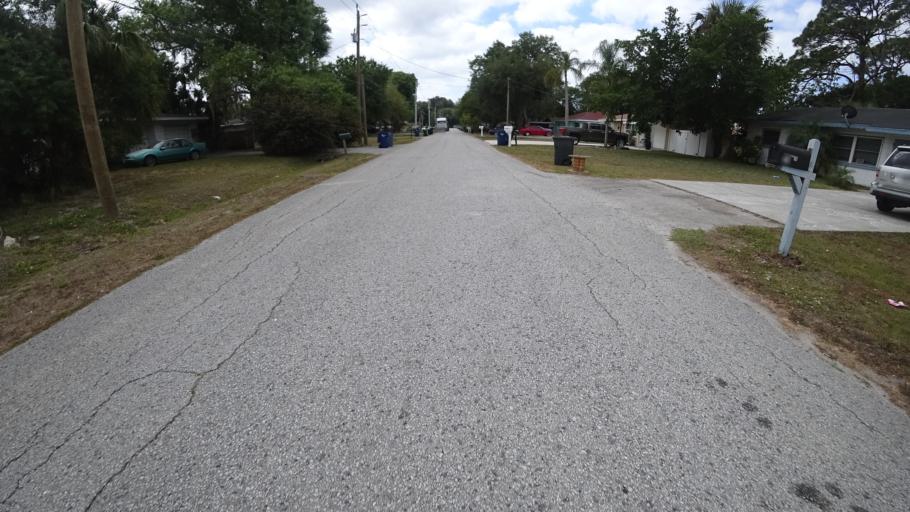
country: US
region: Florida
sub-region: Manatee County
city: South Bradenton
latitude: 27.4470
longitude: -82.5795
